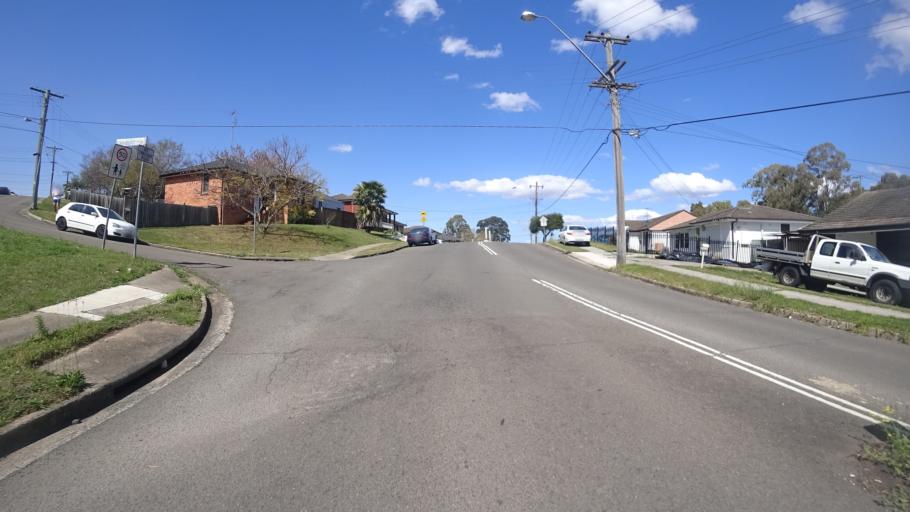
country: AU
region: New South Wales
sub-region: Fairfield
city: Cabramatta West
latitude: -33.9047
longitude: 150.9074
